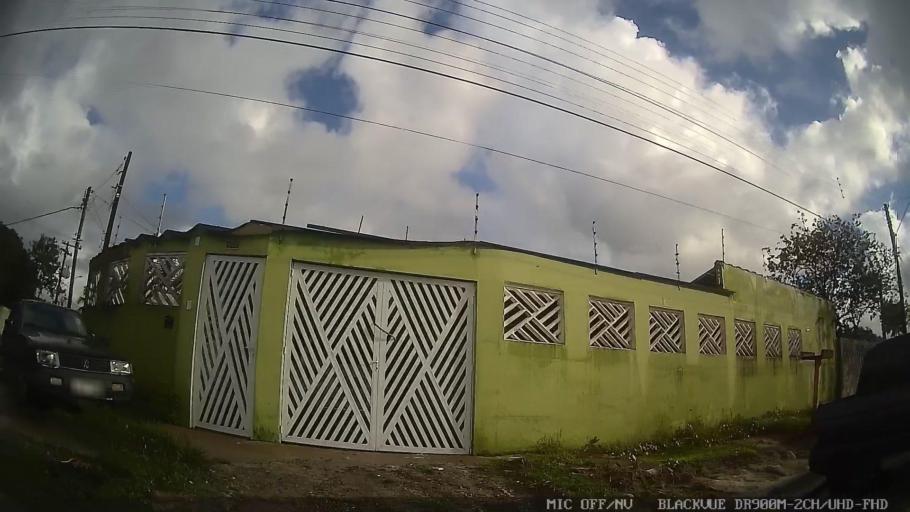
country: BR
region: Sao Paulo
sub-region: Itanhaem
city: Itanhaem
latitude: -24.1765
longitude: -46.8513
